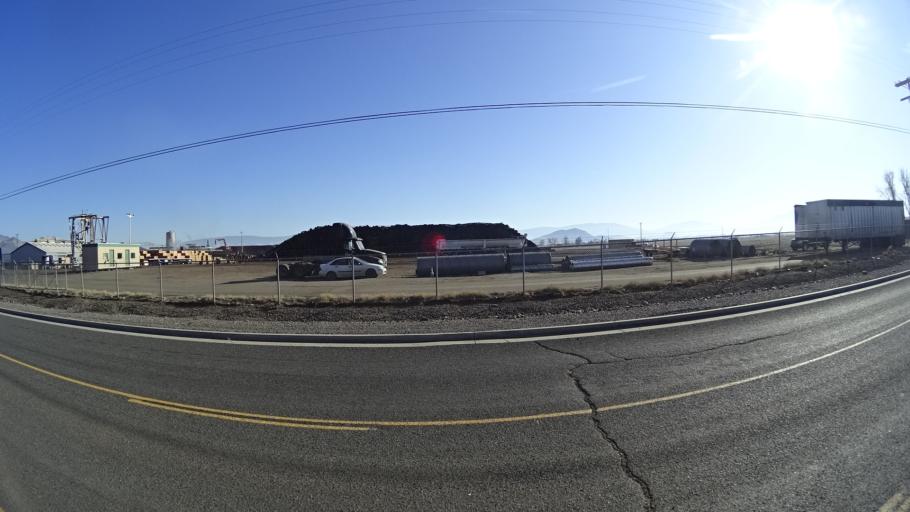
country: US
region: California
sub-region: Siskiyou County
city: Yreka
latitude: 41.7299
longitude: -122.5934
